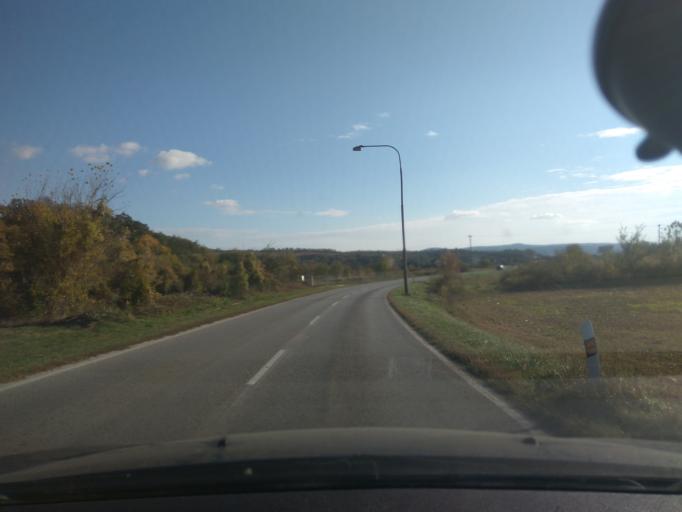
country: SK
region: Trnavsky
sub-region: Okres Trnava
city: Piestany
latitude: 48.5735
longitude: 17.8367
